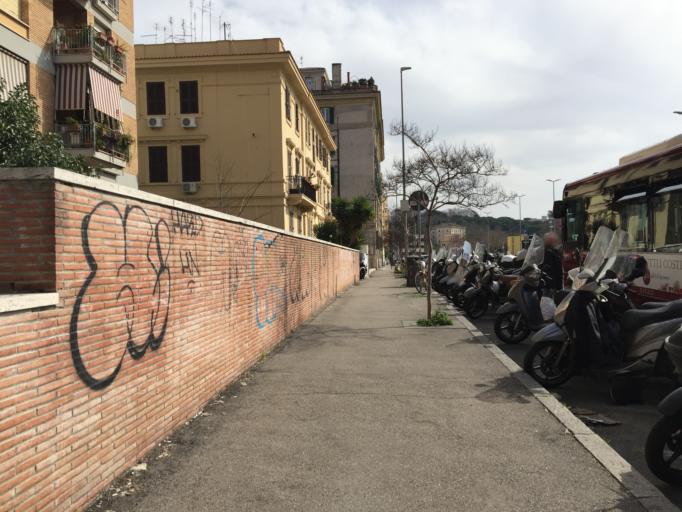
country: VA
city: Vatican City
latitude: 41.8969
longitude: 12.4546
